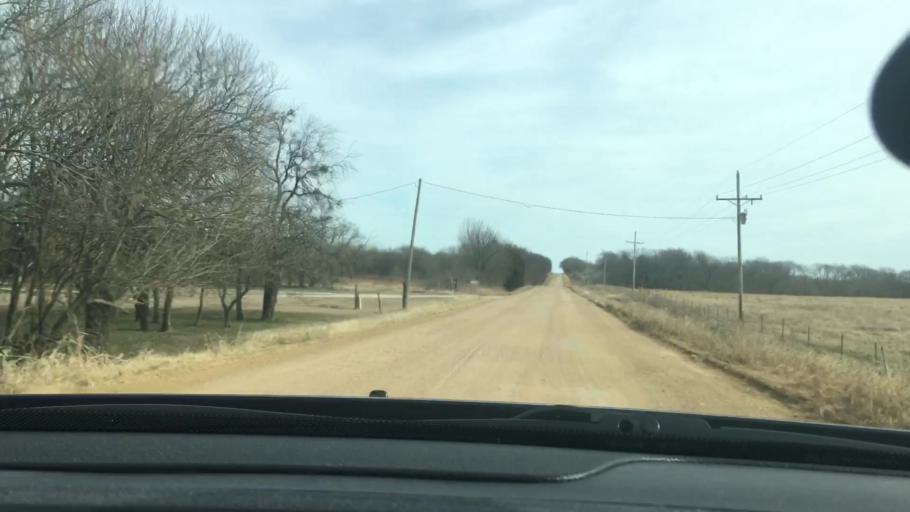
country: US
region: Oklahoma
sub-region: Murray County
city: Sulphur
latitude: 34.4049
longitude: -96.9081
